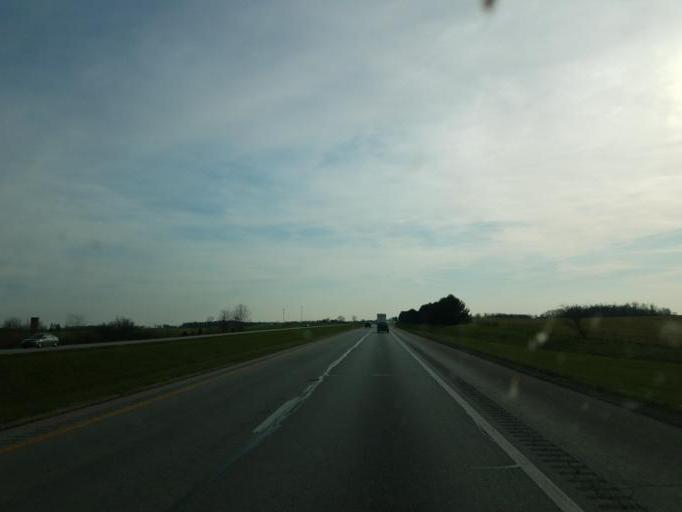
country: US
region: Ohio
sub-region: Greene County
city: Jamestown
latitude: 39.5663
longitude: -83.7050
